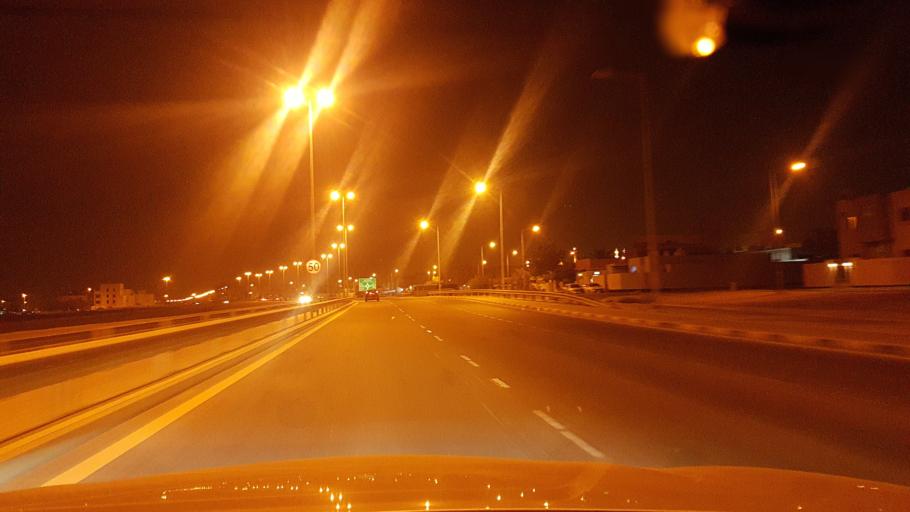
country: BH
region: Central Governorate
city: Madinat Hamad
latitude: 26.0926
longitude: 50.5012
